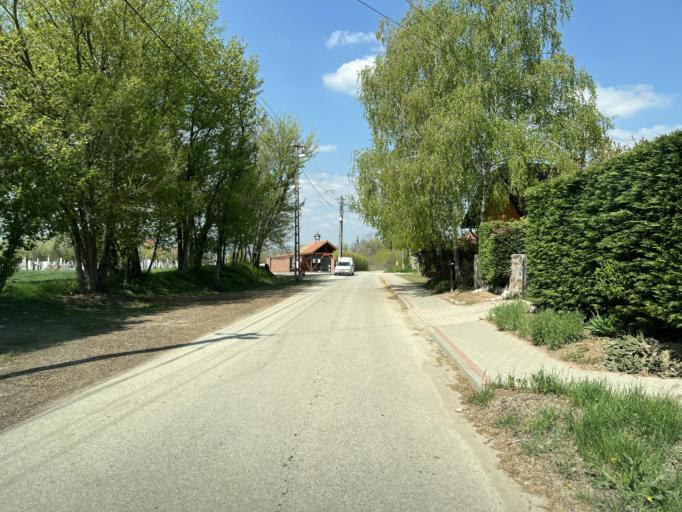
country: HU
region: Pest
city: Fot
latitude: 47.6628
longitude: 19.2255
